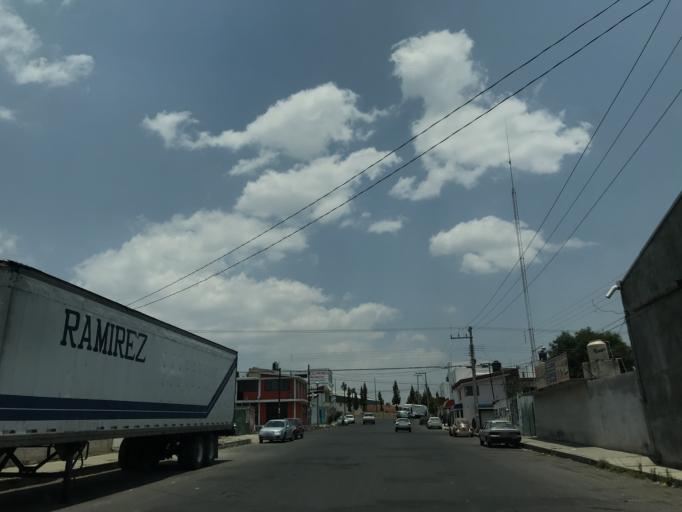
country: MX
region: Tlaxcala
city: Apizaco
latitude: 19.4191
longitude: -98.1511
